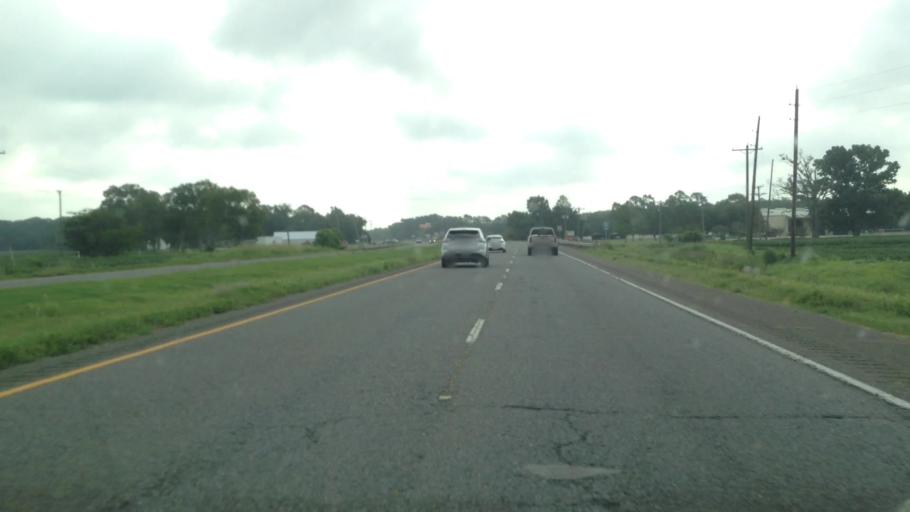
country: US
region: Louisiana
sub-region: Saint Landry Parish
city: Opelousas
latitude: 30.5399
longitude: -92.0322
